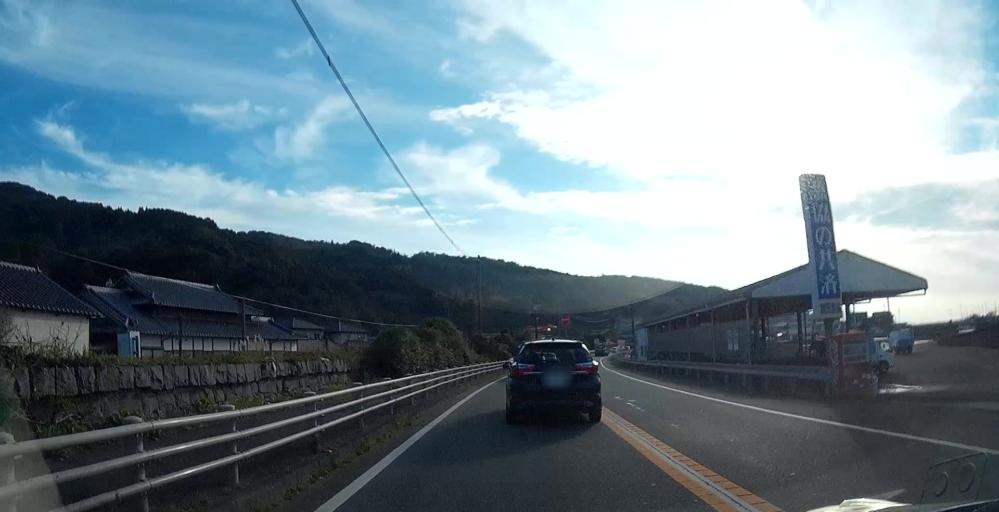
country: JP
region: Kumamoto
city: Uto
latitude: 32.6955
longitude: 130.5658
